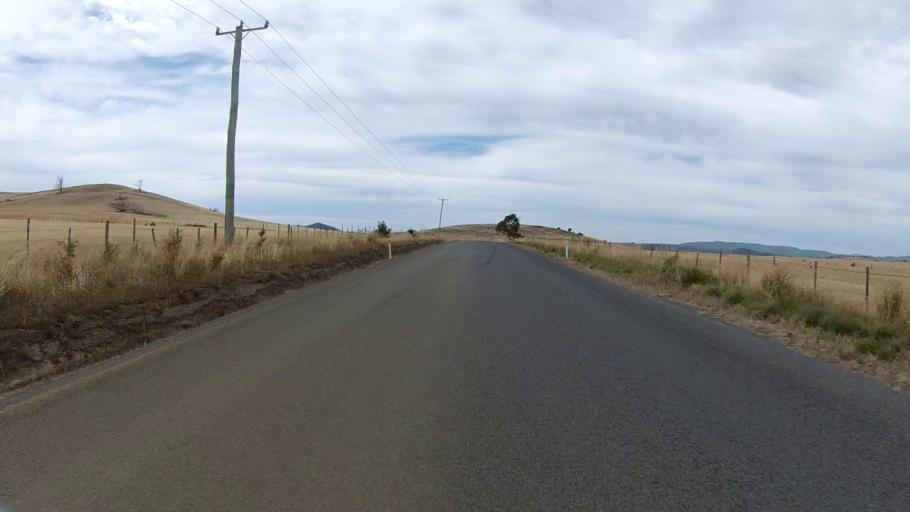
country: AU
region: Tasmania
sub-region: Sorell
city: Sorell
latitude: -42.8977
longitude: 147.7556
